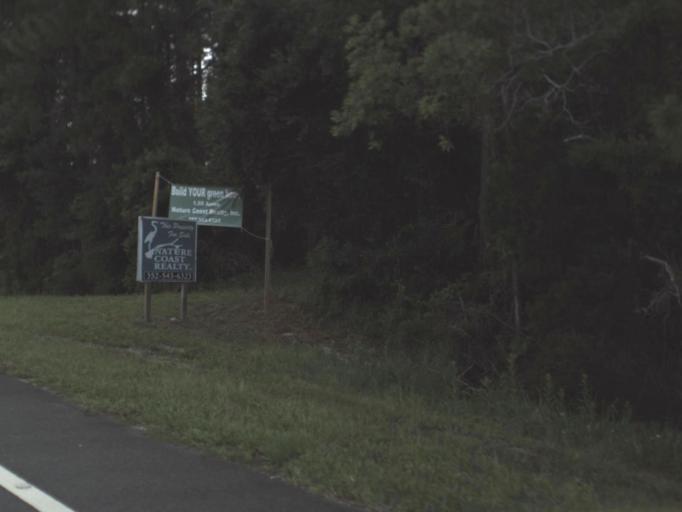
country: US
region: Florida
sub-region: Levy County
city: Chiefland
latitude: 29.1754
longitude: -83.0247
